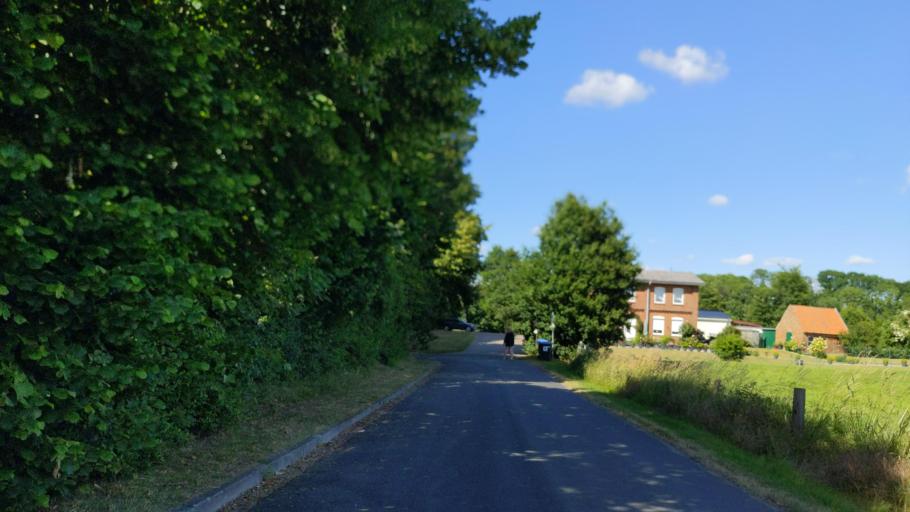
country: DE
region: Schleswig-Holstein
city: Behlendorf
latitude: 53.7013
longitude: 10.6719
